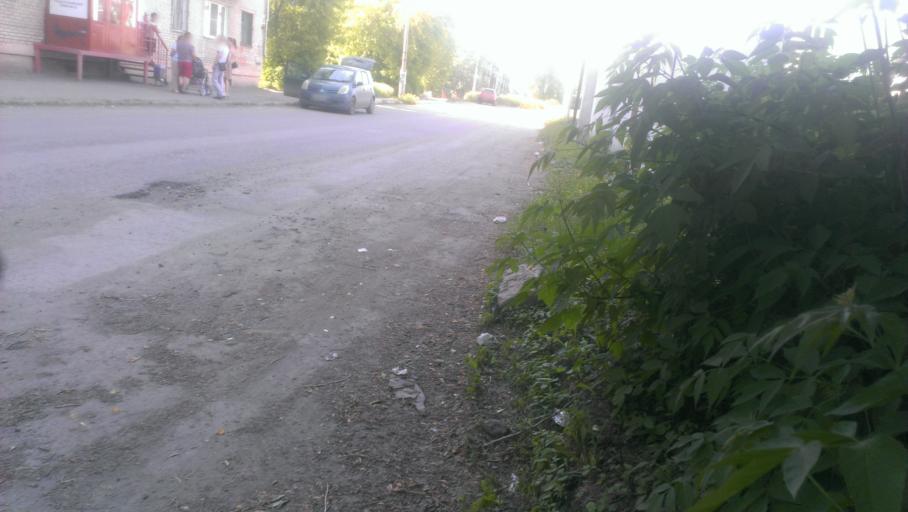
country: RU
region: Altai Krai
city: Novoaltaysk
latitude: 53.3967
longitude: 83.9357
